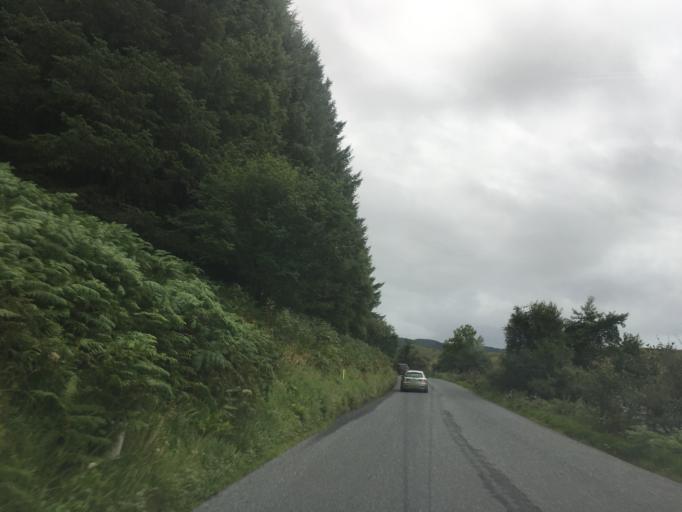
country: GB
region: Scotland
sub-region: Argyll and Bute
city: Oban
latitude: 56.2730
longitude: -5.4779
